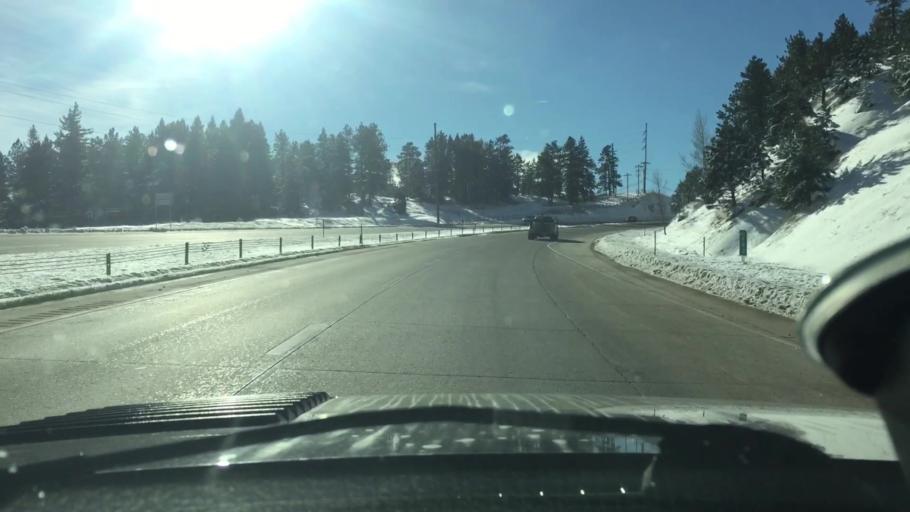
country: US
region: Colorado
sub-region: Jefferson County
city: Indian Hills
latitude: 39.5903
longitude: -105.2213
